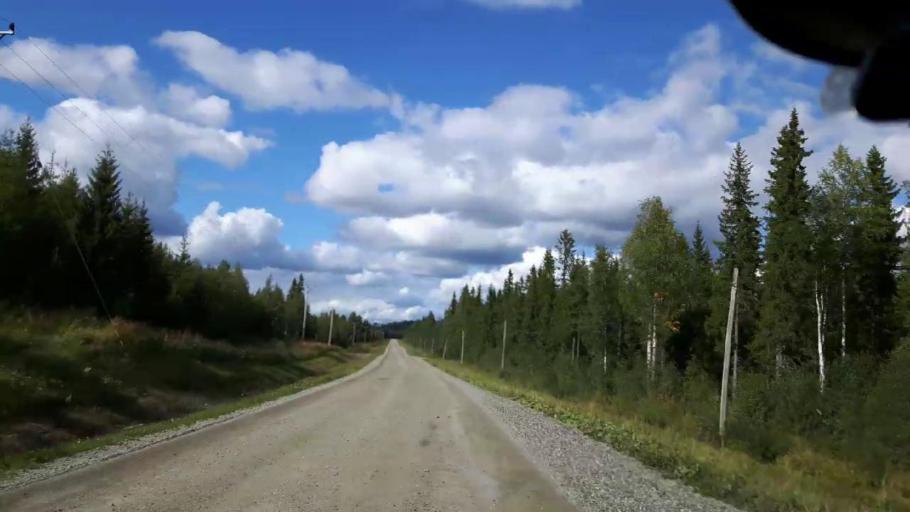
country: SE
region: Jaemtland
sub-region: Stroemsunds Kommun
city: Stroemsund
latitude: 63.3166
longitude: 15.5883
